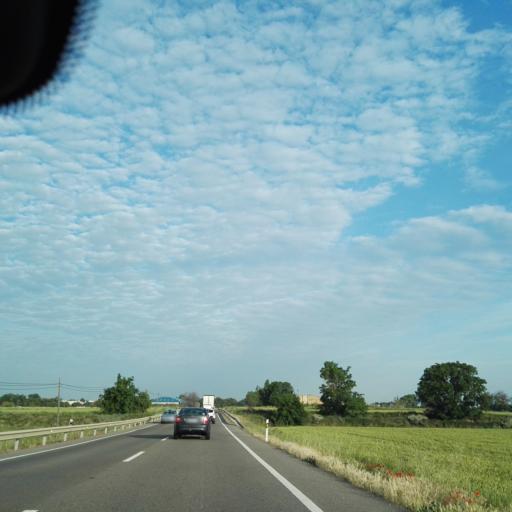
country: ES
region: Aragon
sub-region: Provincia de Zaragoza
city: Oliver-Valdefierro, Oliver, Valdefierro
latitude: 41.6621
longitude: -0.9587
